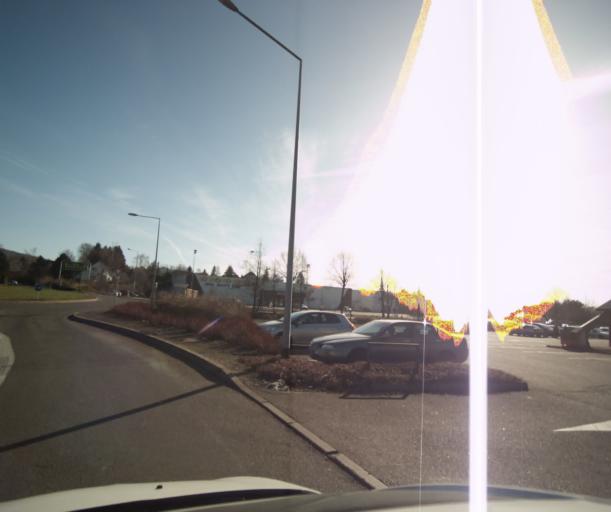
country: FR
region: Franche-Comte
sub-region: Departement du Doubs
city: Avanne-Aveney
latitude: 47.2198
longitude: 5.9551
